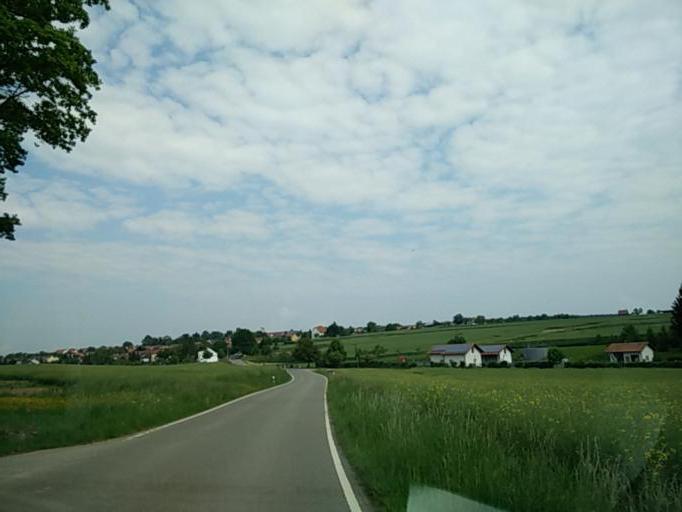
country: DE
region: Baden-Wuerttemberg
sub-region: Tuebingen Region
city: Hirrlingen
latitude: 48.4172
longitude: 8.8520
